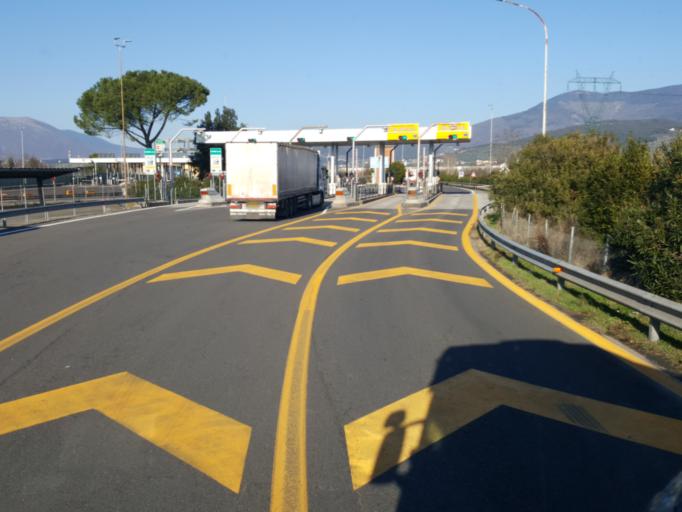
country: IT
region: Tuscany
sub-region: Province of Florence
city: Calenzano
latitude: 43.8332
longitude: 11.1609
